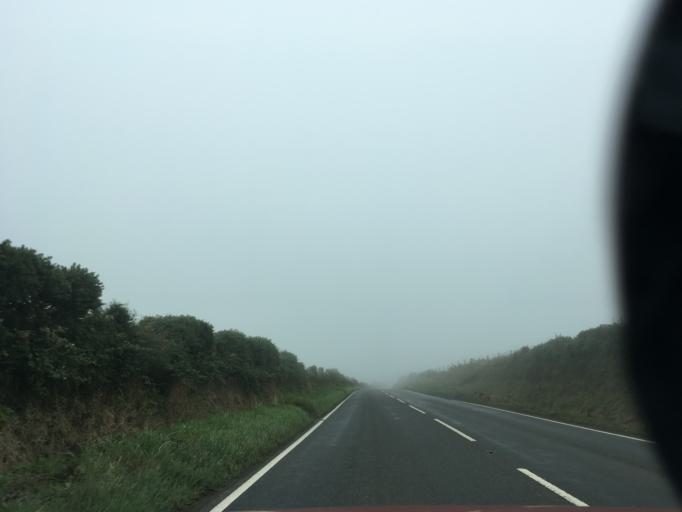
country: GB
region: Wales
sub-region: Pembrokeshire
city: Llanrhian
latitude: 51.8688
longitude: -5.1390
